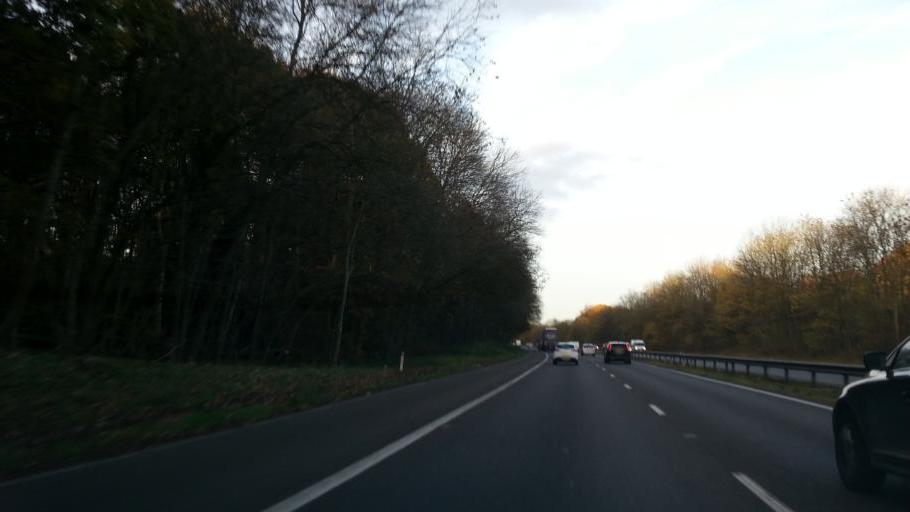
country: GB
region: England
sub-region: Hertfordshire
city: Welwyn
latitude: 51.8483
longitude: -0.1979
